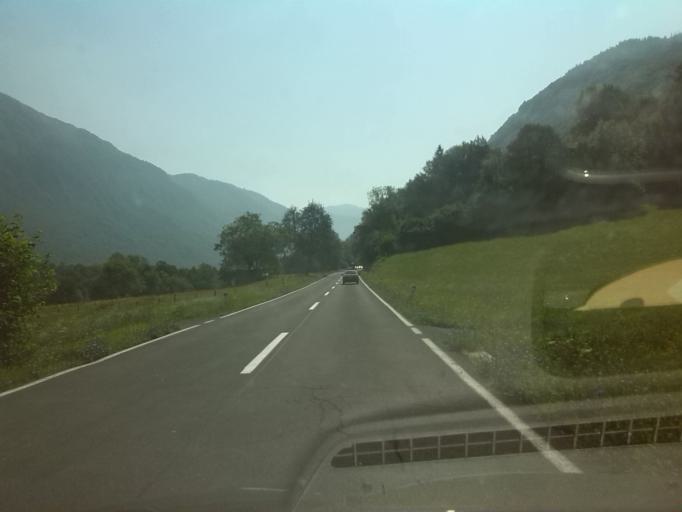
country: IT
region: Friuli Venezia Giulia
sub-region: Provincia di Udine
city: Cras
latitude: 46.2056
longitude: 13.6459
